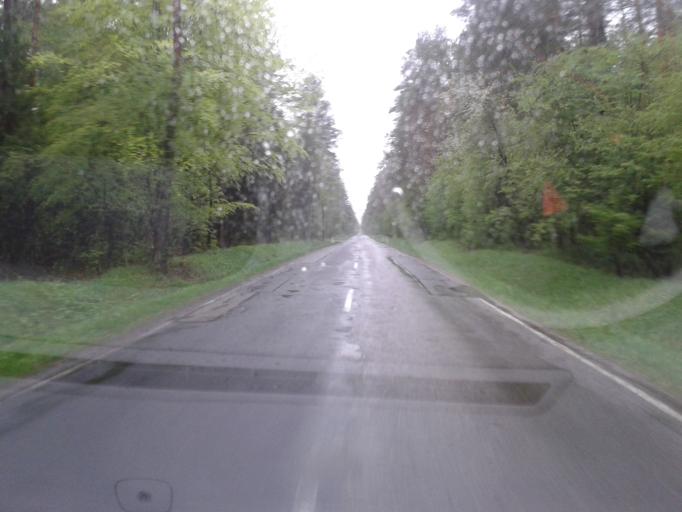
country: PL
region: Subcarpathian Voivodeship
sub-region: Powiat lubaczowski
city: Nowe Siolo
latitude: 50.3009
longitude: 23.2188
